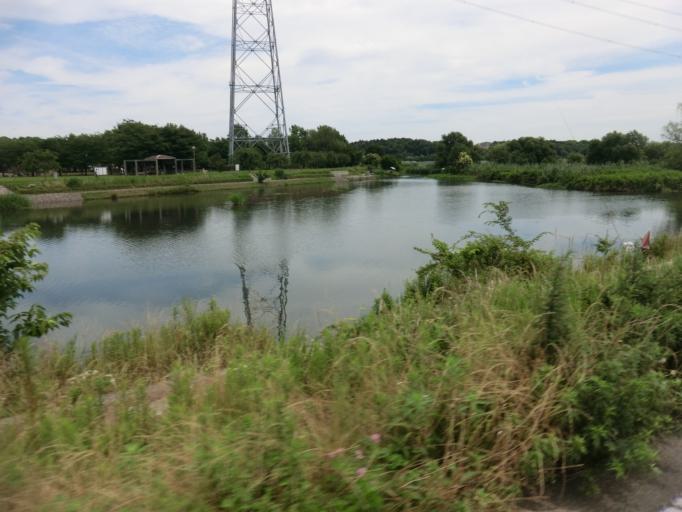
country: JP
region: Chiba
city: Kashiwa
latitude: 35.8671
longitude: 139.9896
